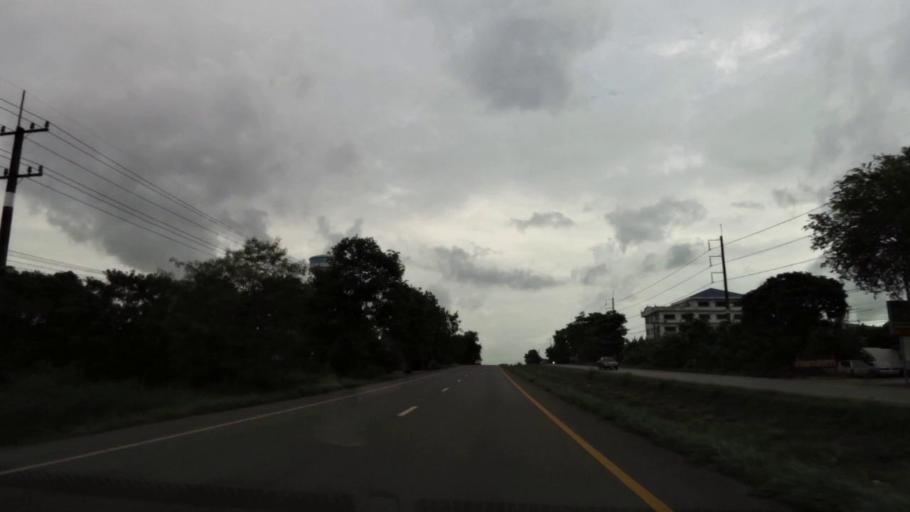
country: TH
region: Chanthaburi
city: Tha Mai
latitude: 12.7027
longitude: 101.9852
